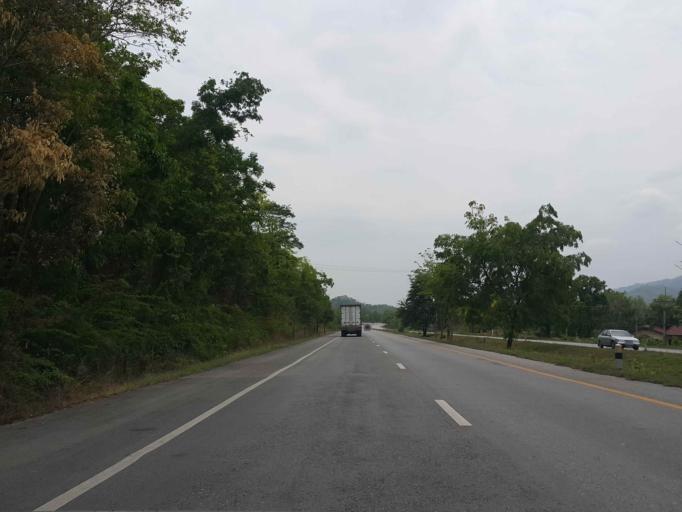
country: TH
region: Lampang
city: Sop Prap
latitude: 17.8586
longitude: 99.3079
